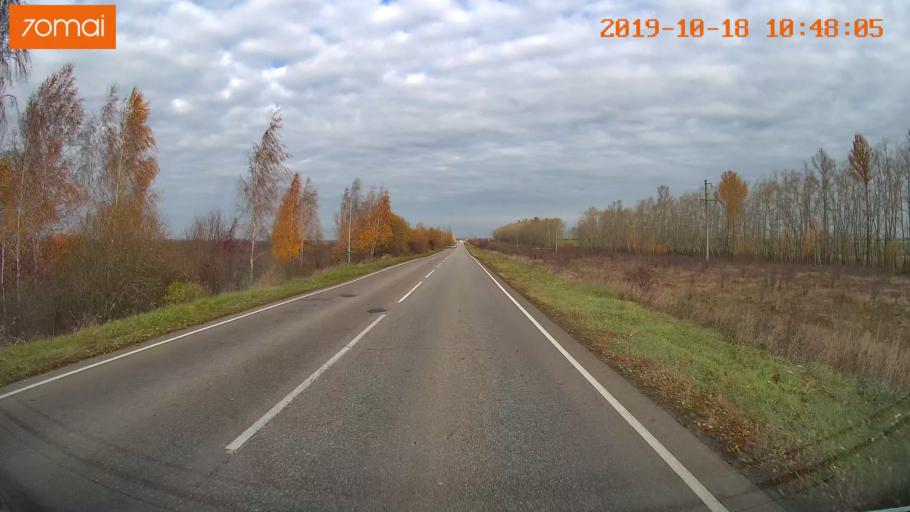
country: RU
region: Tula
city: Yepifan'
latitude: 53.7111
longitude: 38.6974
